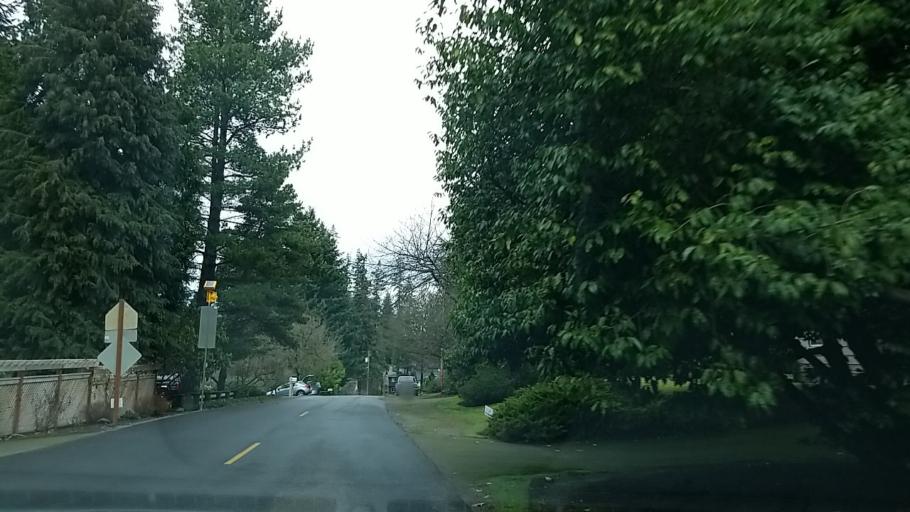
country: US
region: Washington
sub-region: Snohomish County
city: Esperance
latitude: 47.7857
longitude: -122.3585
